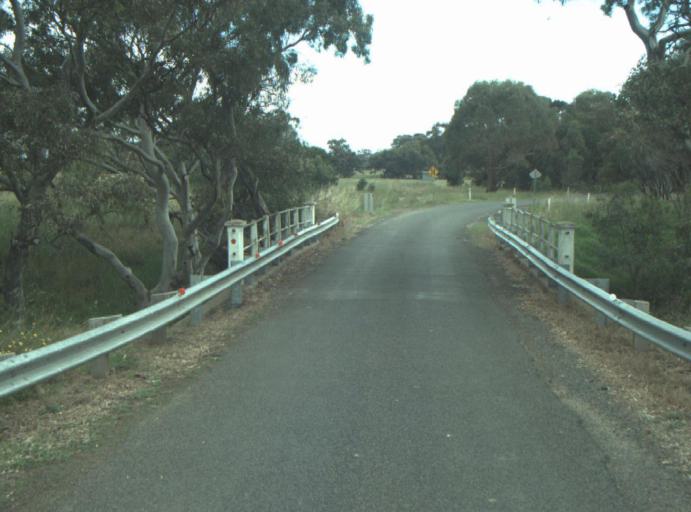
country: AU
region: Victoria
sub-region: Greater Geelong
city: Lara
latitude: -37.8453
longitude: 144.3545
